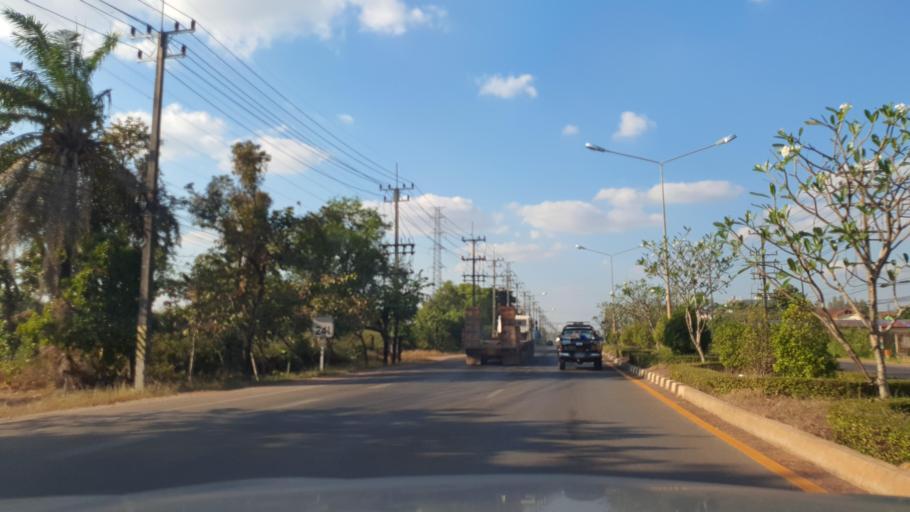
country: TH
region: Sakon Nakhon
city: Sakon Nakhon
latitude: 17.1429
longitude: 104.1103
